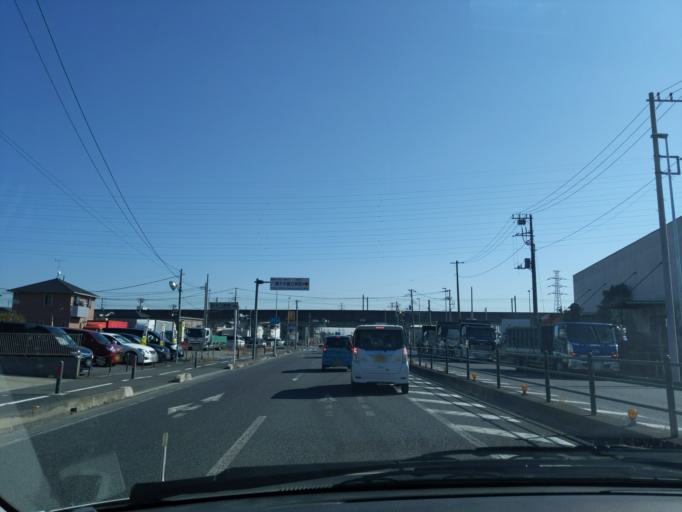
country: JP
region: Saitama
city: Yashio-shi
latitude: 35.8157
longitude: 139.8539
